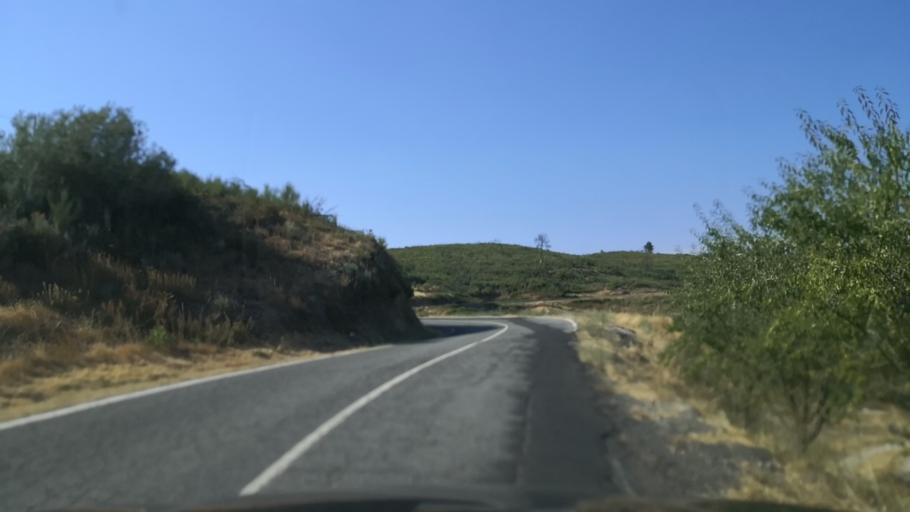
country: PT
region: Vila Real
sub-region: Sabrosa
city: Sabrosa
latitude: 41.3015
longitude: -7.4753
